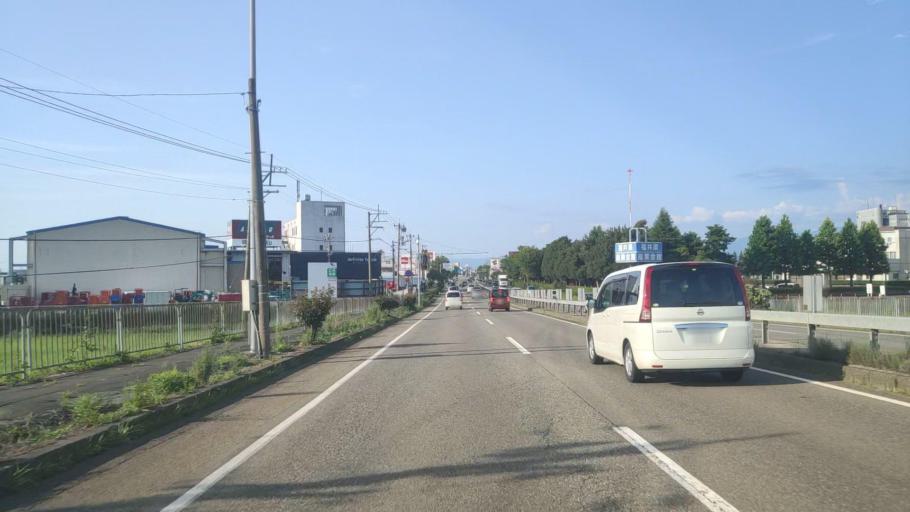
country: JP
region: Fukui
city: Fukui-shi
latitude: 36.0359
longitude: 136.2285
